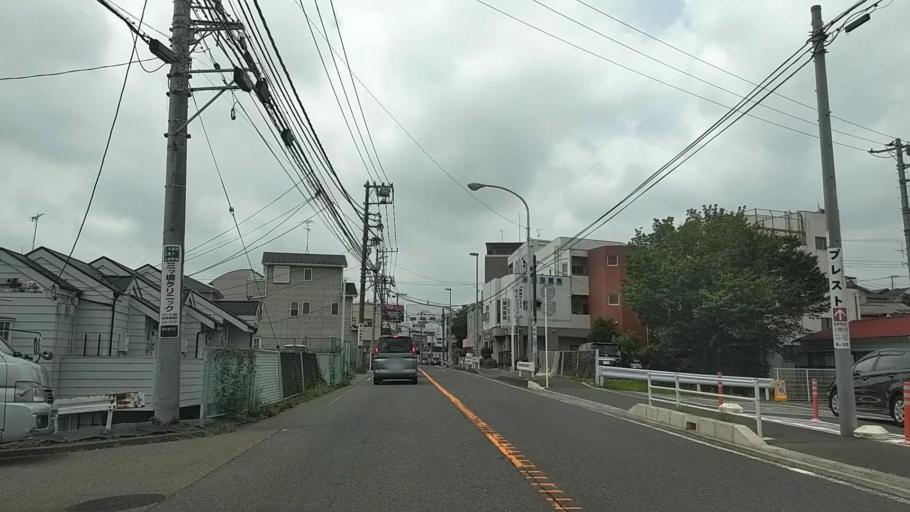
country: JP
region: Kanagawa
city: Minami-rinkan
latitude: 35.4613
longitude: 139.5174
